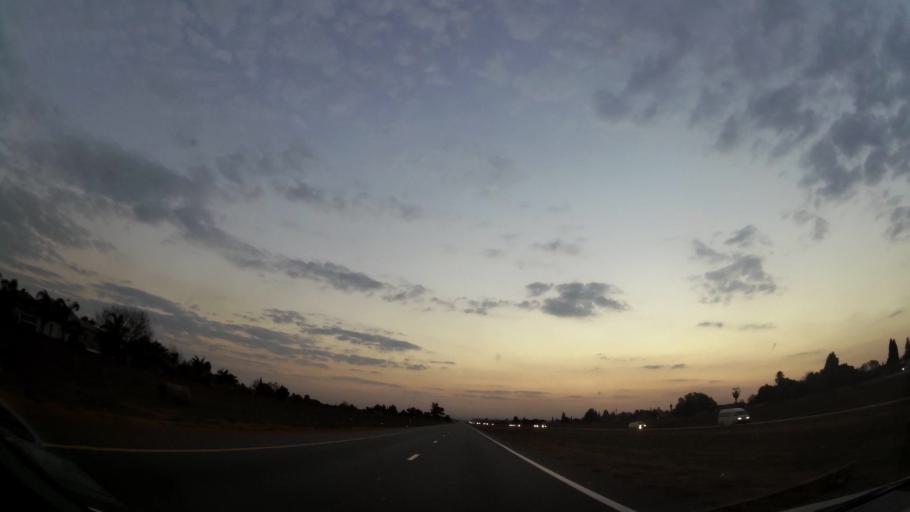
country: ZA
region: Gauteng
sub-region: Ekurhuleni Metropolitan Municipality
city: Boksburg
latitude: -26.2521
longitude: 28.2828
